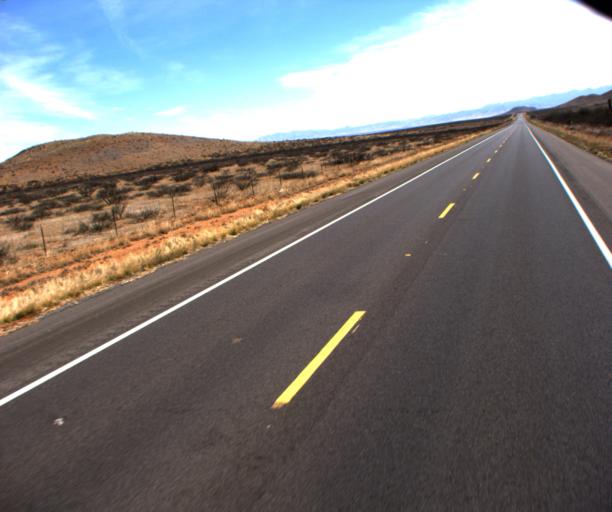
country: US
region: Arizona
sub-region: Cochise County
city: Tombstone
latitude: 31.9054
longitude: -109.7776
